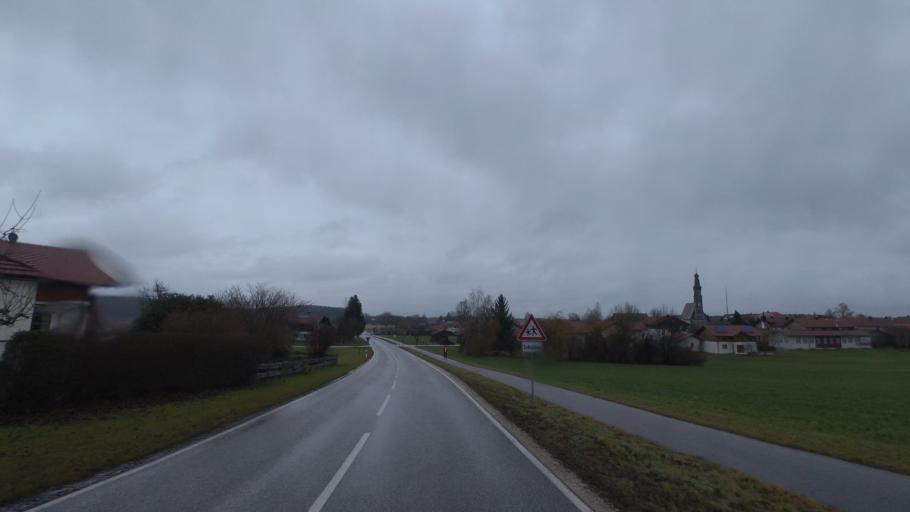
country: DE
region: Bavaria
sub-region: Upper Bavaria
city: Petting
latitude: 47.9409
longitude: 12.8022
